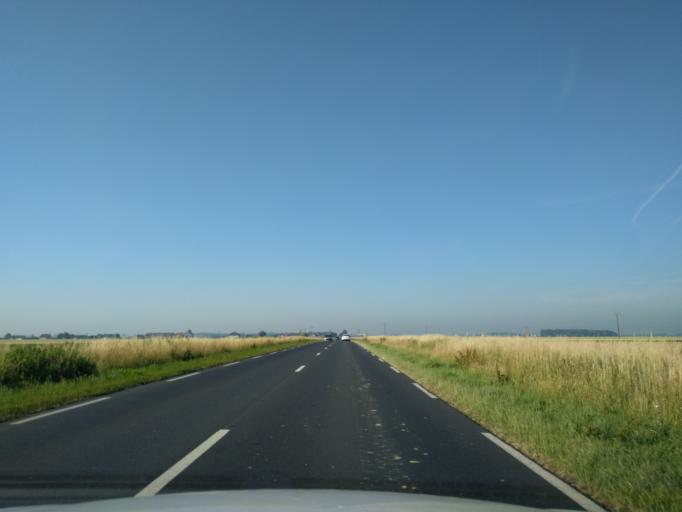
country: FR
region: Picardie
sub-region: Departement de la Somme
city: Roye
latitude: 49.7358
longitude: 2.8073
